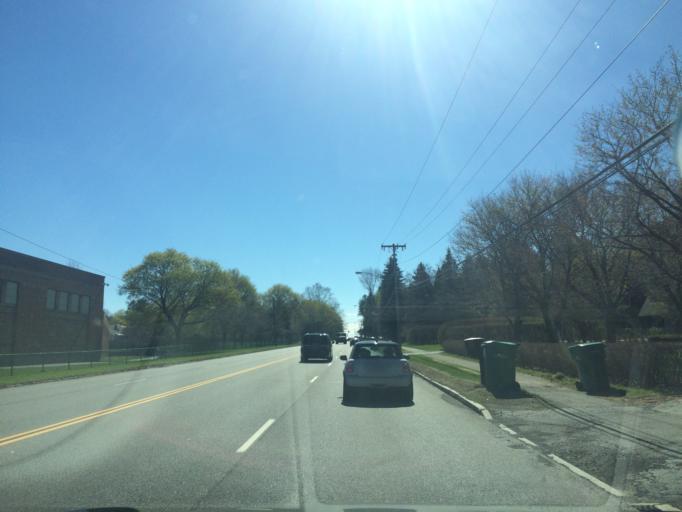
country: US
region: New York
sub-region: Monroe County
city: East Rochester
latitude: 43.1063
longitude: -77.4937
